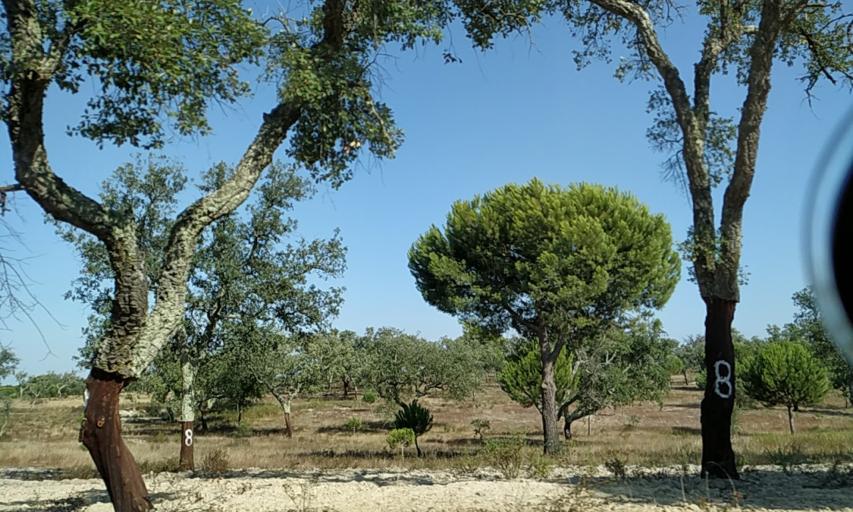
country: PT
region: Santarem
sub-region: Coruche
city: Coruche
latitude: 38.8443
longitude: -8.5533
